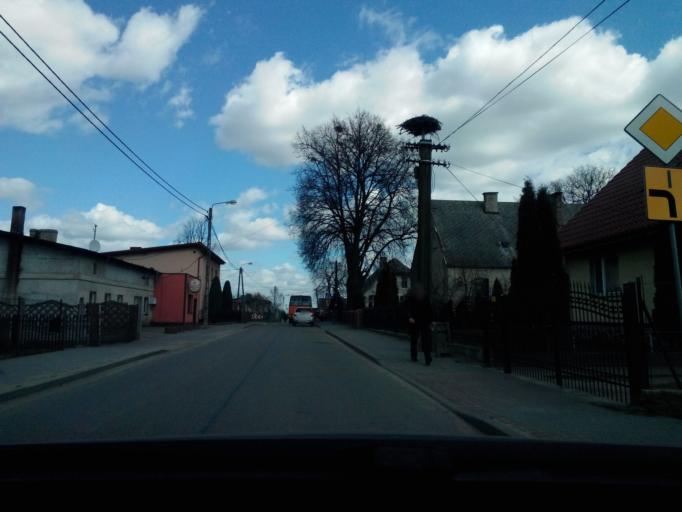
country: PL
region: Warmian-Masurian Voivodeship
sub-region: Powiat nowomiejski
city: Biskupiec
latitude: 53.4703
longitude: 19.3188
